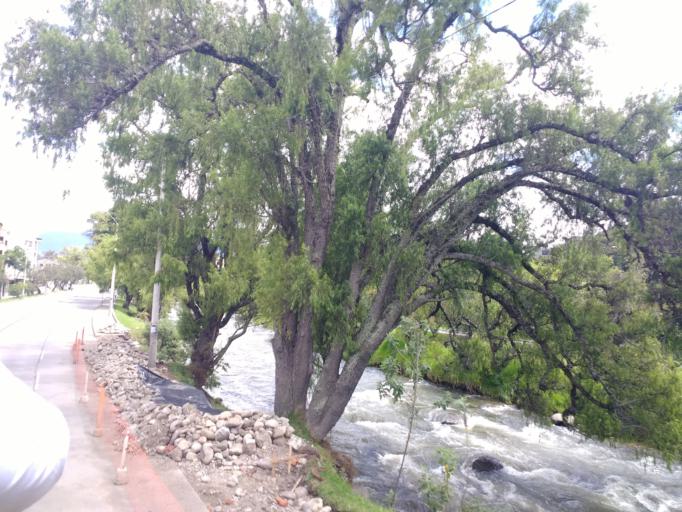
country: EC
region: Azuay
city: Cuenca
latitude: -2.9088
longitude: -78.9978
